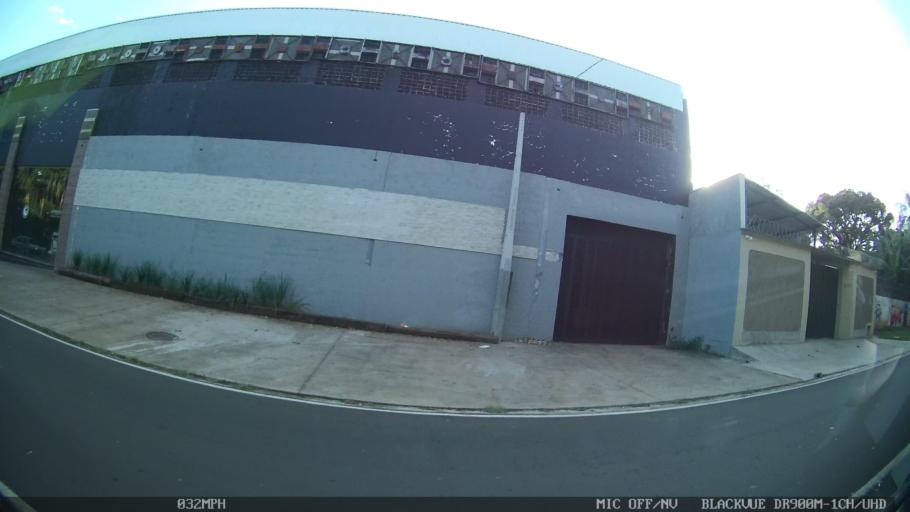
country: BR
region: Sao Paulo
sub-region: Piracicaba
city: Piracicaba
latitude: -22.7118
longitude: -47.6526
